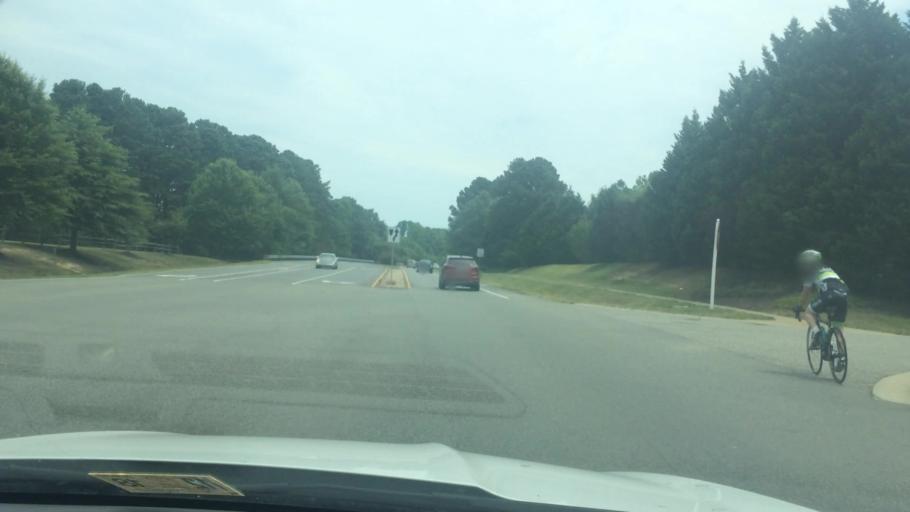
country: US
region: Virginia
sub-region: James City County
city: Williamsburg
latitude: 37.2665
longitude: -76.7666
